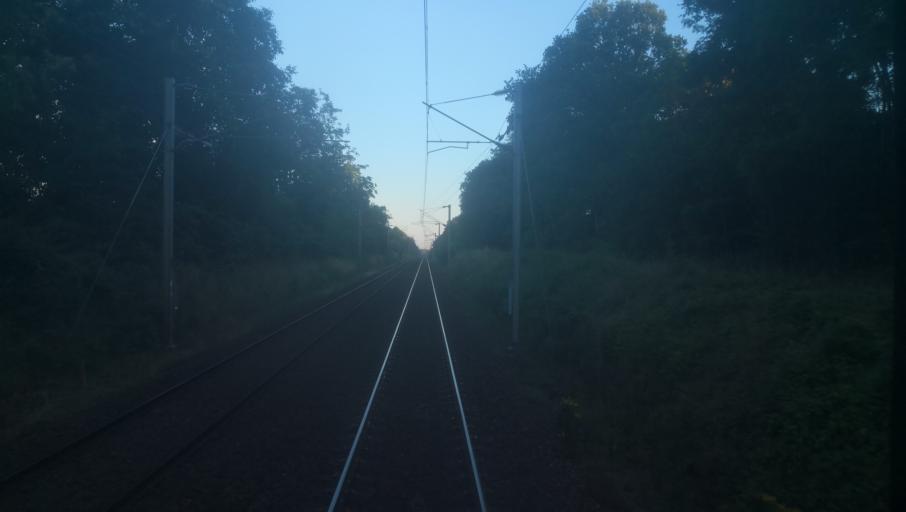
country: FR
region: Bourgogne
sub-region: Departement de la Nievre
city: La Charite-sur-Loire
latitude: 47.2199
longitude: 3.0171
